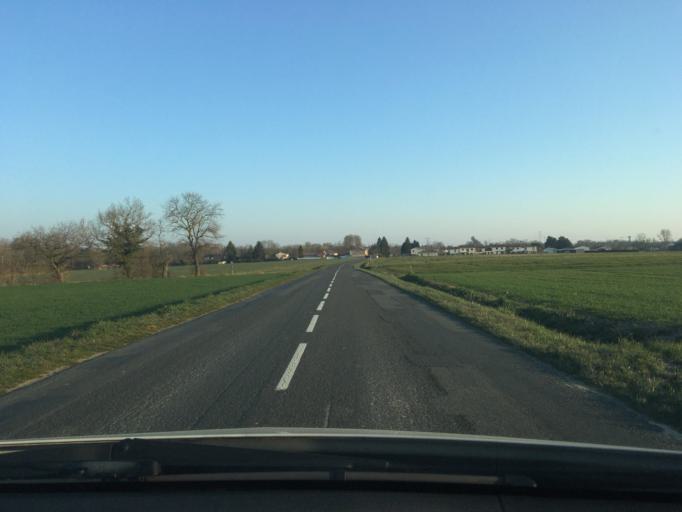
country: FR
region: Rhone-Alpes
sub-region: Departement de l'Ain
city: Saint-Andre-de-Corcy
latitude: 45.9479
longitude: 4.9388
